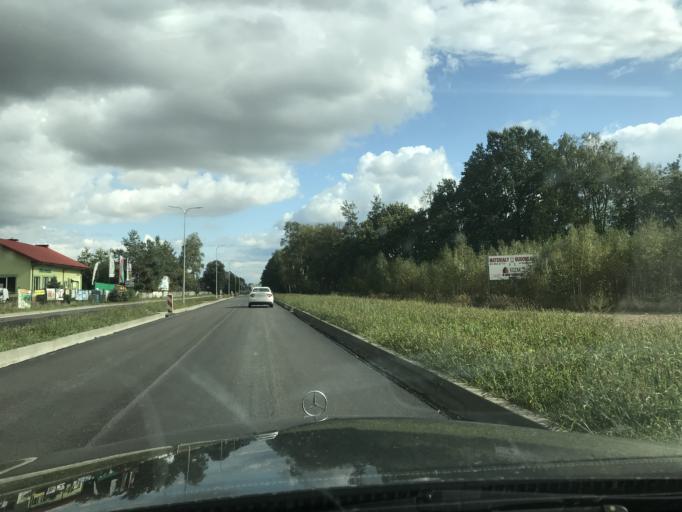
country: PL
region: Lublin Voivodeship
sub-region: Powiat lubartowski
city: Lubartow
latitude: 51.4774
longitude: 22.5957
